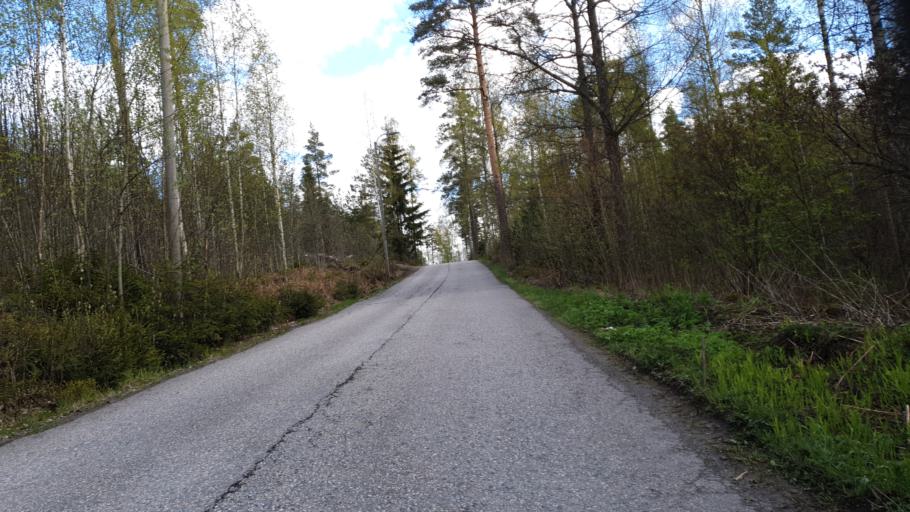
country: FI
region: Uusimaa
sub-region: Helsinki
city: Nurmijaervi
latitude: 60.3470
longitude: 24.8416
